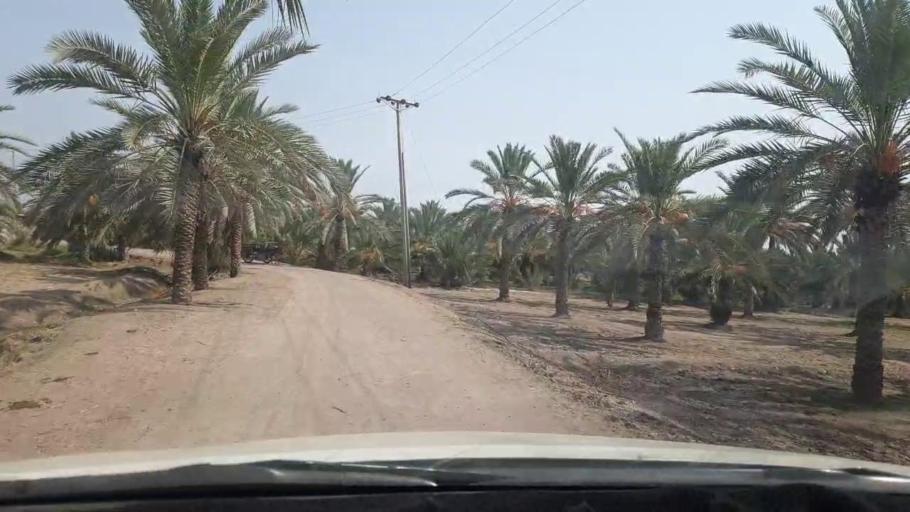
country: PK
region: Sindh
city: Rohri
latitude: 27.6275
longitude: 68.8872
